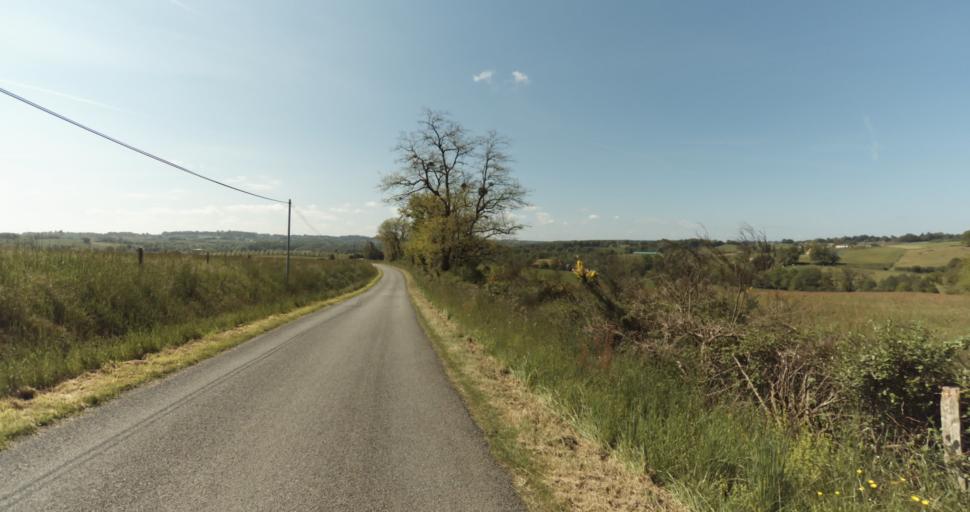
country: FR
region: Limousin
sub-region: Departement de la Haute-Vienne
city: Le Vigen
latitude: 45.7059
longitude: 1.3008
